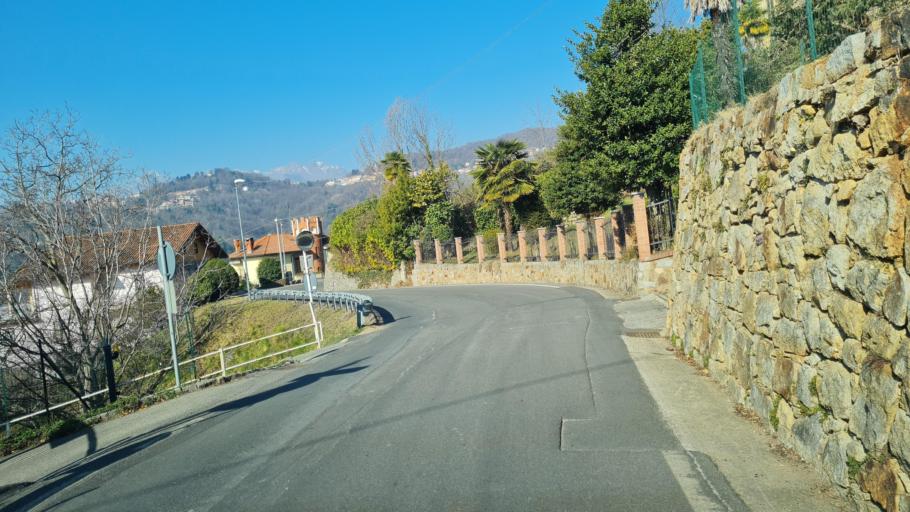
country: IT
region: Piedmont
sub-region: Provincia di Biella
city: Valle San Nicolao
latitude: 45.6054
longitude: 8.1307
